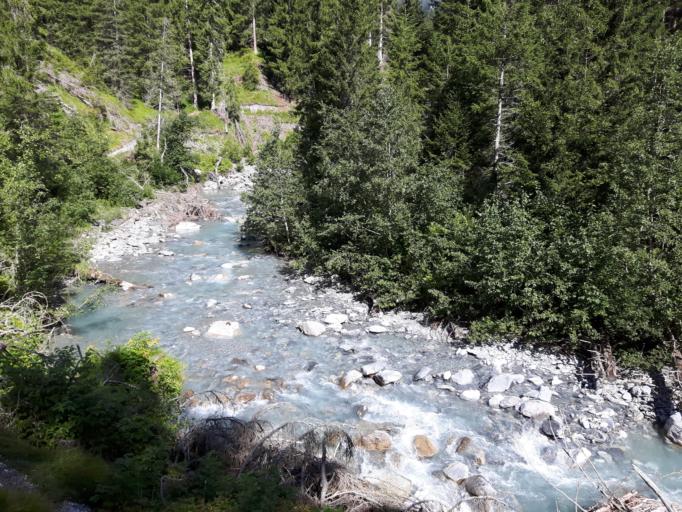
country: CH
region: Grisons
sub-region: Imboden District
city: Flims
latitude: 46.8425
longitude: 9.2638
